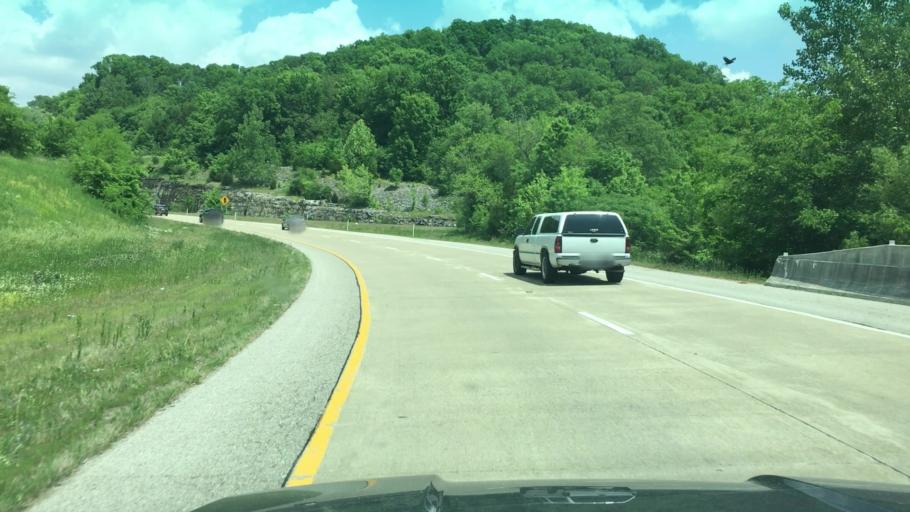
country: US
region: Tennessee
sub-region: Williamson County
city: Thompson's Station
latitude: 35.8232
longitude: -86.8339
